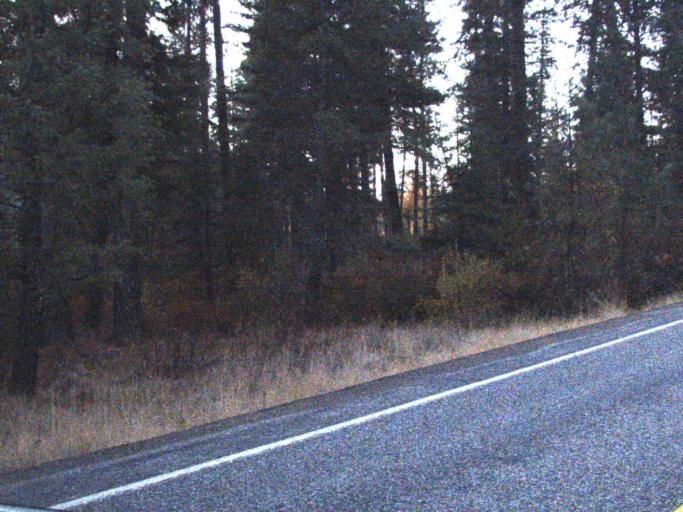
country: US
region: Washington
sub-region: Ferry County
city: Republic
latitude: 48.3423
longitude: -118.7479
